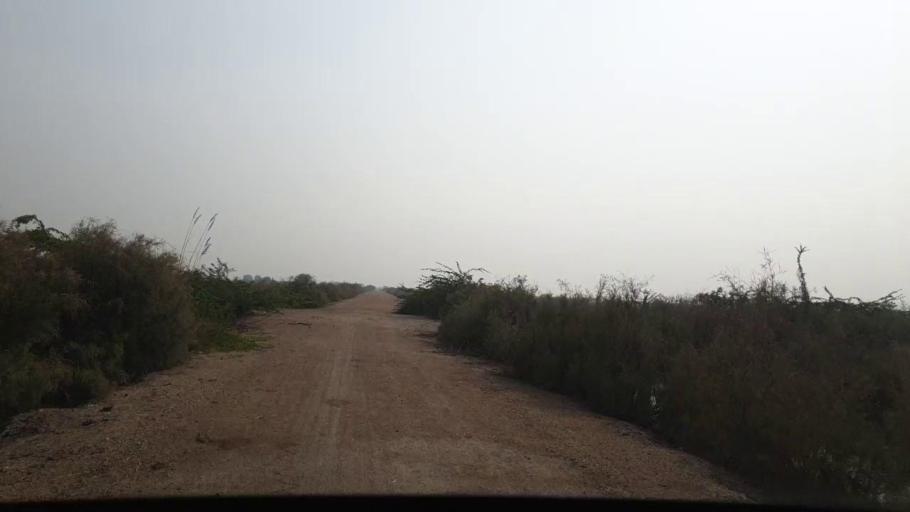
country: PK
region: Sindh
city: Jati
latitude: 24.2739
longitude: 68.4232
